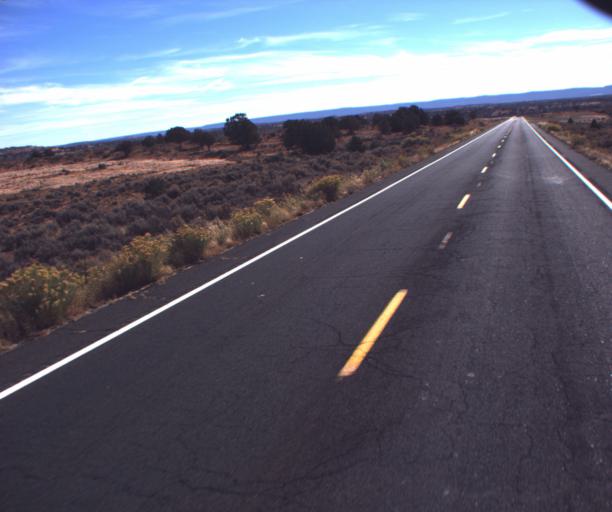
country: US
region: Arizona
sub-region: Coconino County
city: Kaibito
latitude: 36.5643
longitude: -110.7560
